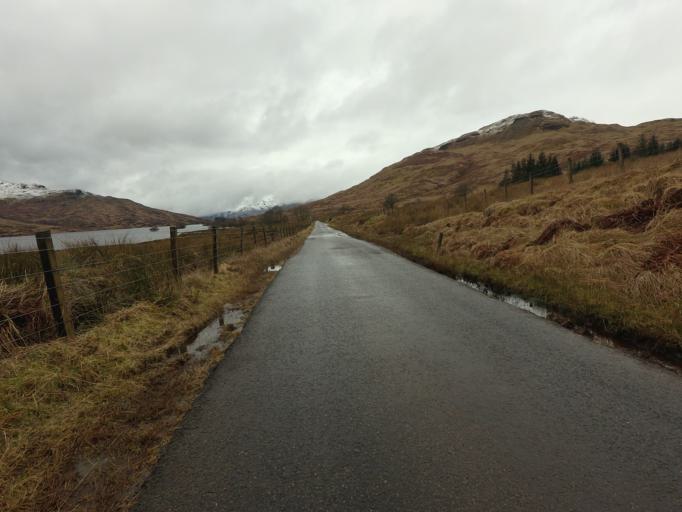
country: GB
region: Scotland
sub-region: West Dunbartonshire
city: Balloch
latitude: 56.2495
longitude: -4.6197
